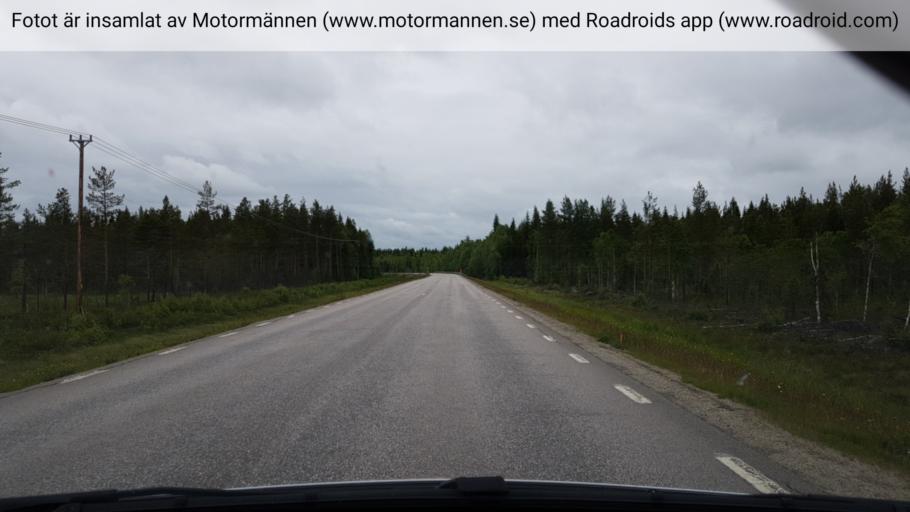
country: SE
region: Vaesterbotten
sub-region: Vannas Kommun
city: Vaennaes
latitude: 64.0412
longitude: 19.6888
